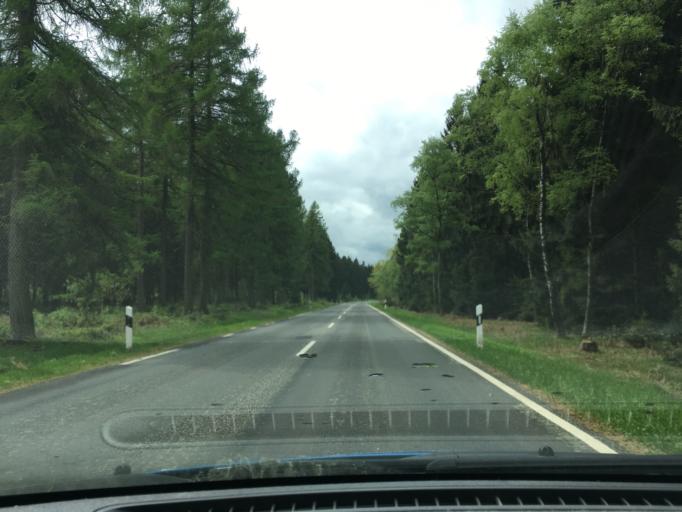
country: DE
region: Lower Saxony
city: Heinade
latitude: 51.7760
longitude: 9.5886
